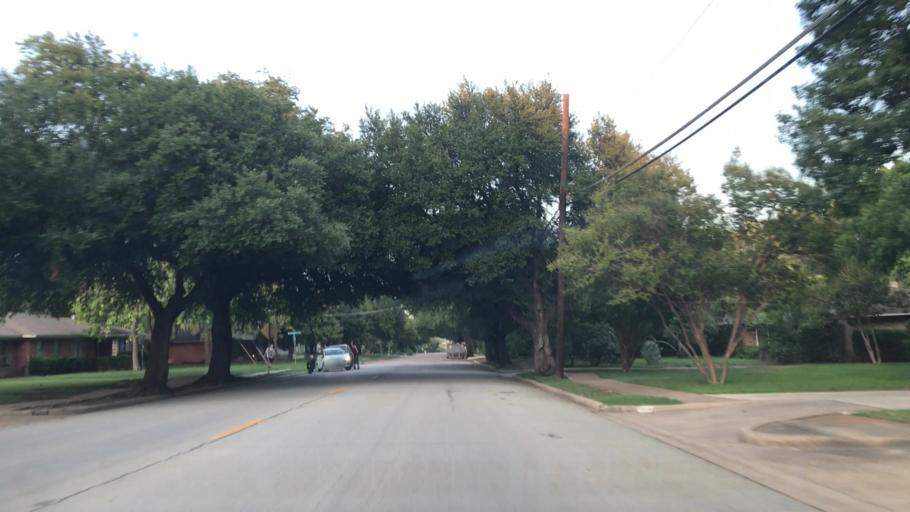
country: US
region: Texas
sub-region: Dallas County
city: University Park
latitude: 32.9006
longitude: -96.7789
